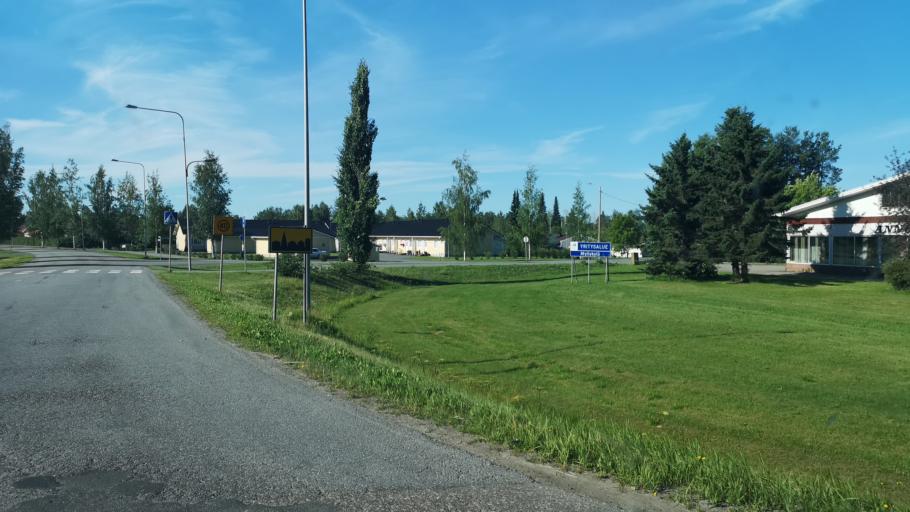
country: FI
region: Southern Ostrobothnia
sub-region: Seinaejoki
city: Lapua
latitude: 62.9690
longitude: 23.0376
